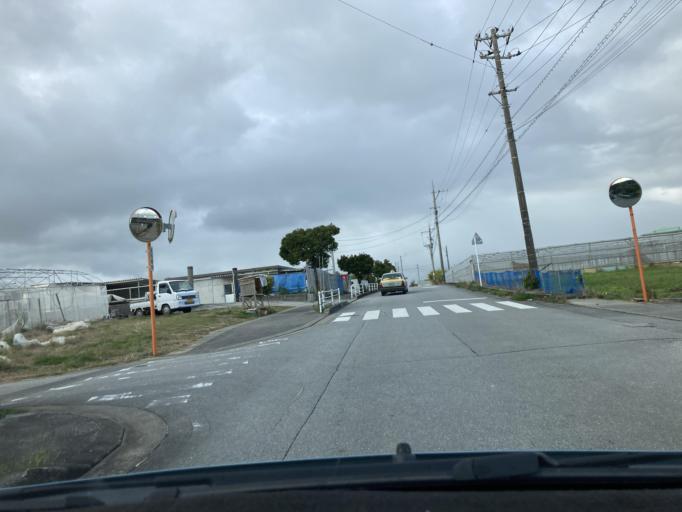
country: JP
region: Okinawa
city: Itoman
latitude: 26.1248
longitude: 127.6866
